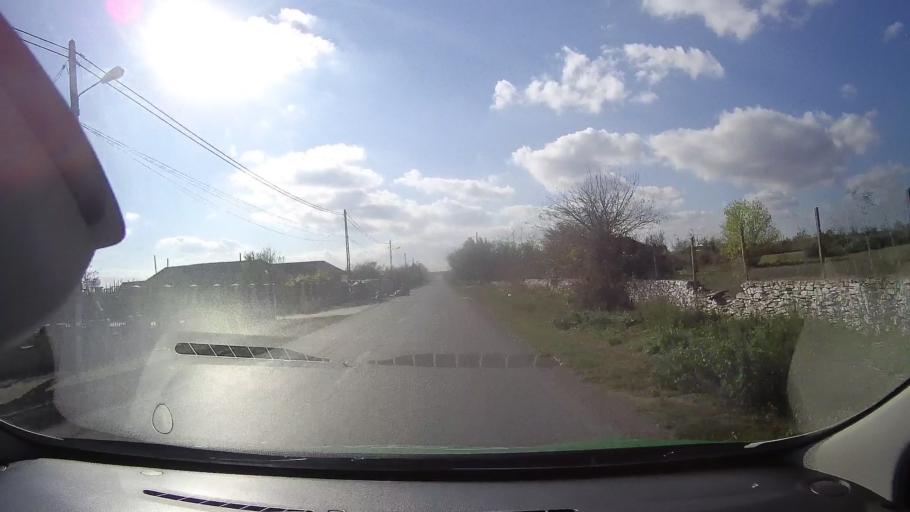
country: RO
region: Constanta
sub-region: Comuna Mihai Viteazu
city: Mihai Viteazu
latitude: 44.6248
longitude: 28.7310
